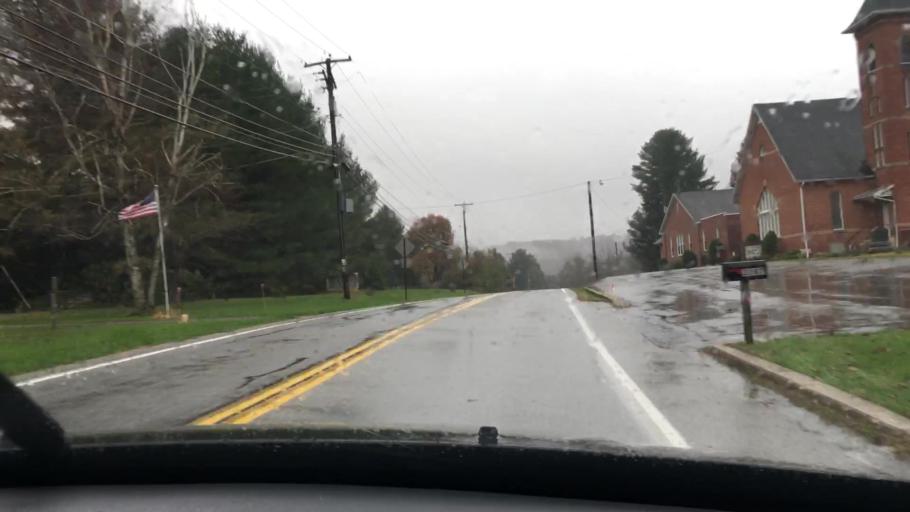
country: US
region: Pennsylvania
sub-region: York County
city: Glen Rock
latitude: 39.7672
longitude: -76.7348
